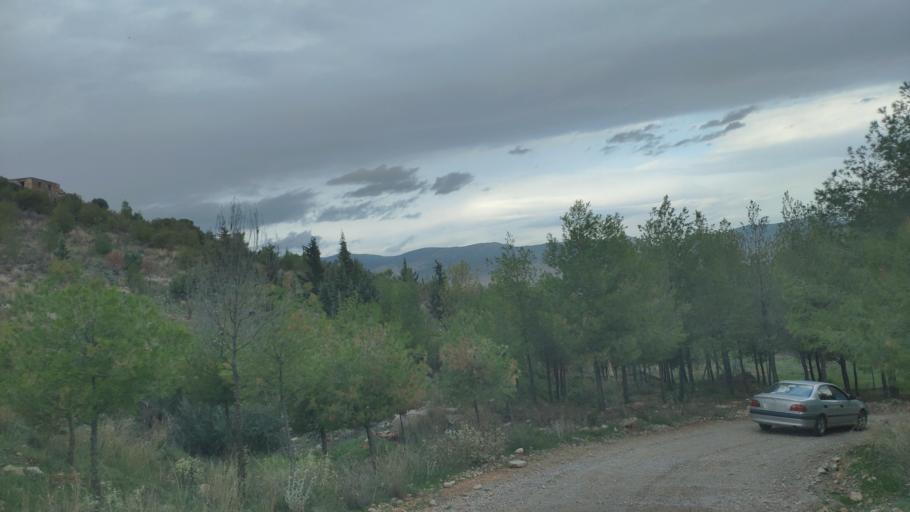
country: GR
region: Attica
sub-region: Nomarchia Dytikis Attikis
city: Megara
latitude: 37.9752
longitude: 23.3686
